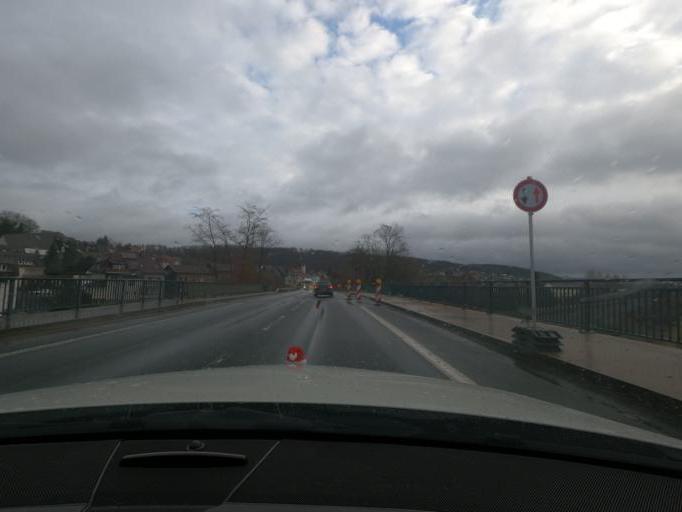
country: DE
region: Lower Saxony
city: Kreiensen
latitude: 51.8580
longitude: 9.9549
